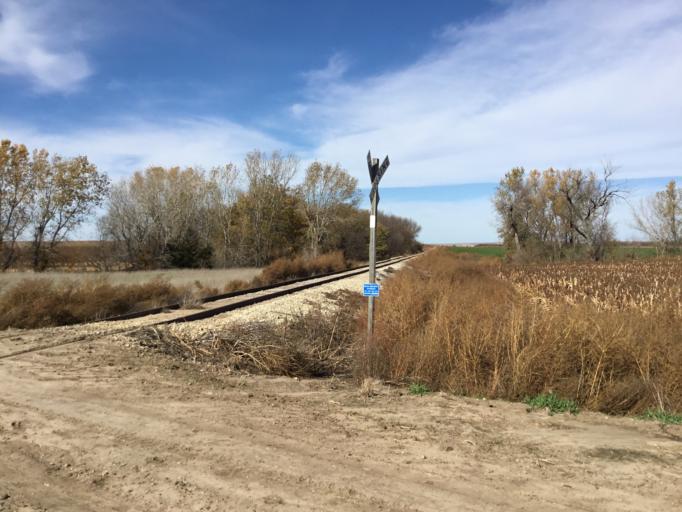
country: US
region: Kansas
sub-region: Lincoln County
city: Lincoln
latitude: 38.9438
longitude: -98.0182
